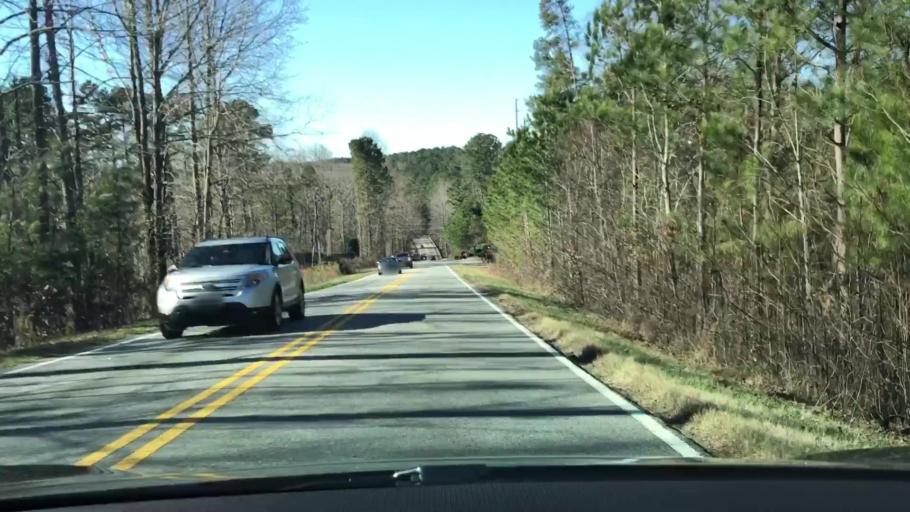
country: US
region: Georgia
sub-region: Forsyth County
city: Cumming
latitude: 34.1855
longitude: -84.1102
